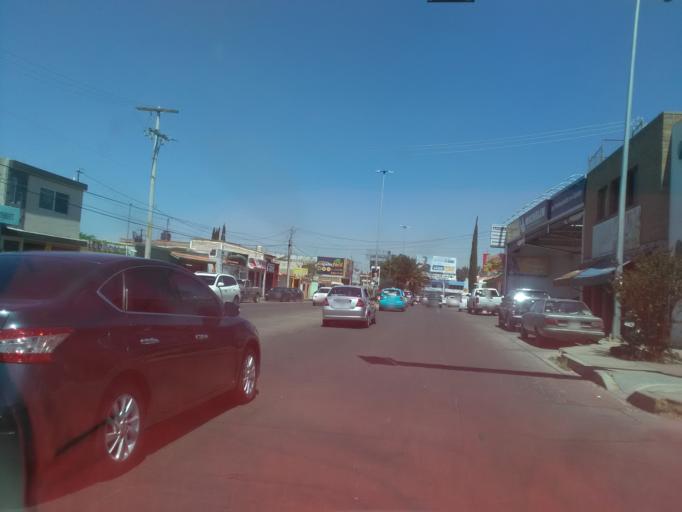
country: MX
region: Durango
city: Victoria de Durango
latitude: 24.0138
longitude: -104.6754
